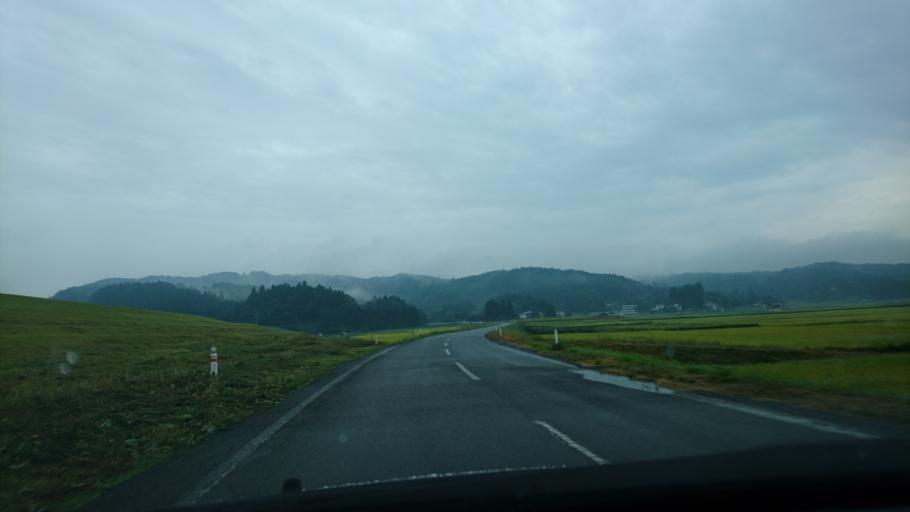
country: JP
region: Iwate
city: Ichinoseki
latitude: 38.8839
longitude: 141.2587
